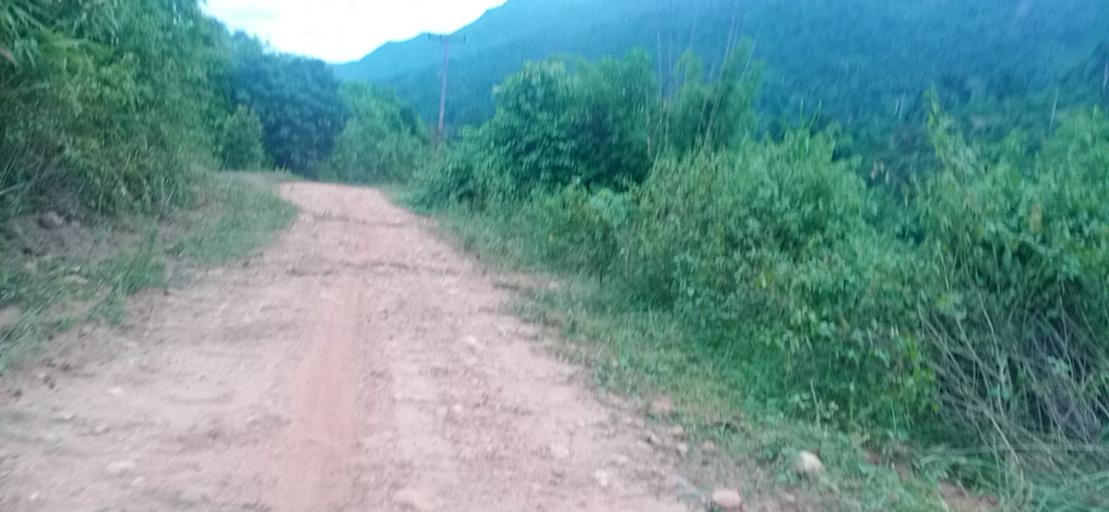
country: TH
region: Changwat Bueng Kan
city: Pak Khat
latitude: 18.5590
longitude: 103.2340
